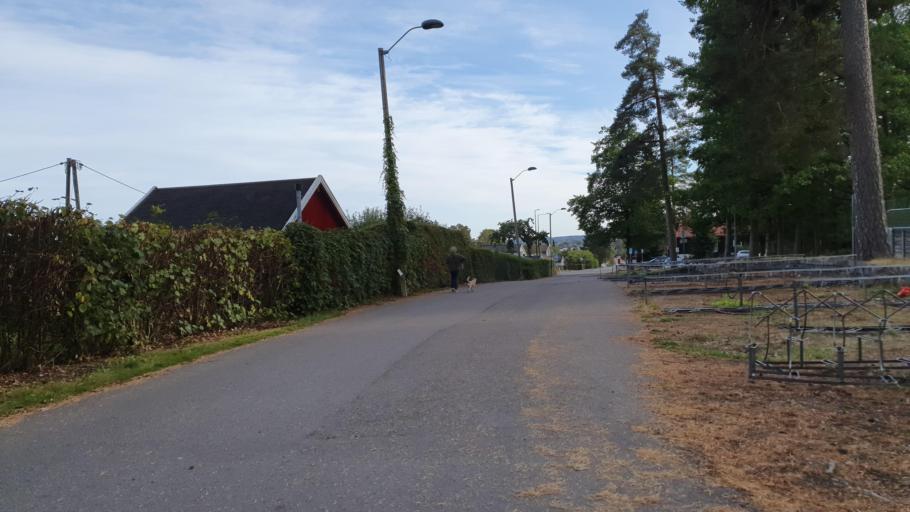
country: NO
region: Vestfold
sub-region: Tonsberg
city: Tonsberg
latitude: 59.2826
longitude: 10.4196
